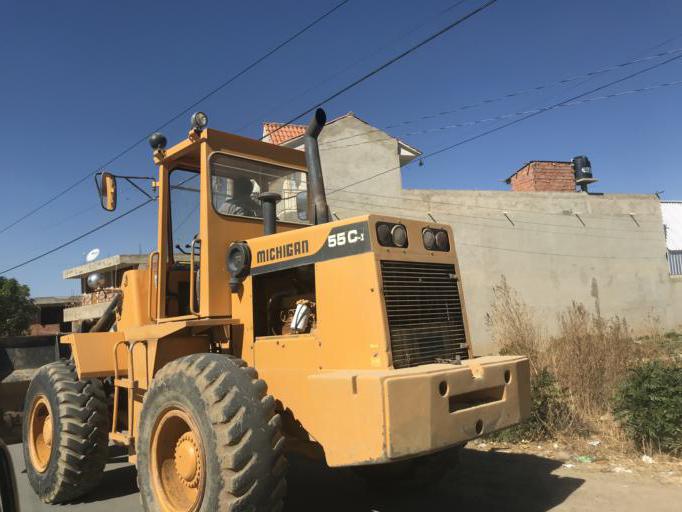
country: BO
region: Cochabamba
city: Cliza
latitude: -17.5876
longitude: -65.9220
